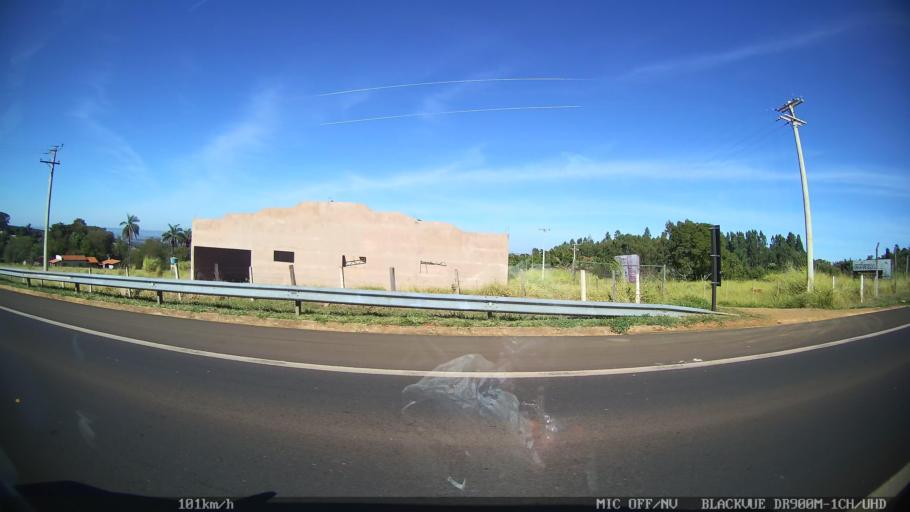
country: BR
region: Sao Paulo
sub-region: Franca
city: Franca
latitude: -20.5785
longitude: -47.3438
